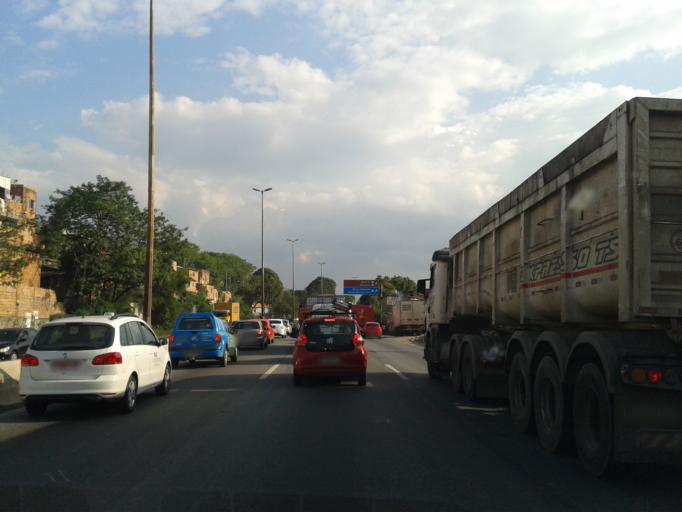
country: BR
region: Minas Gerais
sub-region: Belo Horizonte
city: Belo Horizonte
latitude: -19.8740
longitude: -43.9496
